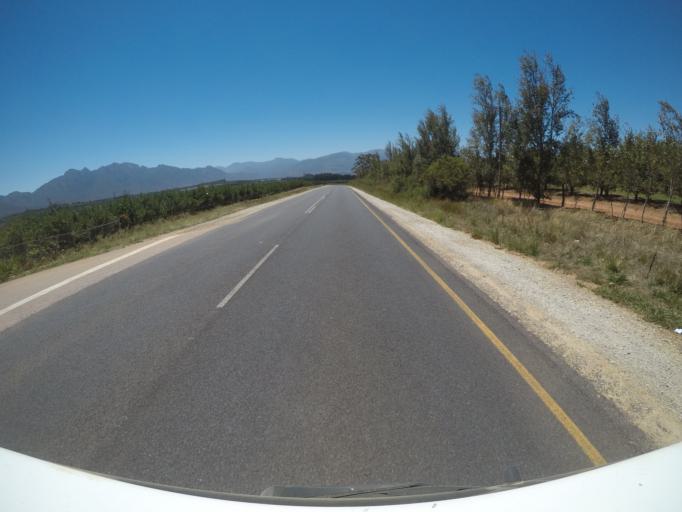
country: ZA
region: Western Cape
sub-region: Overberg District Municipality
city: Grabouw
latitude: -34.0614
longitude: 19.1355
